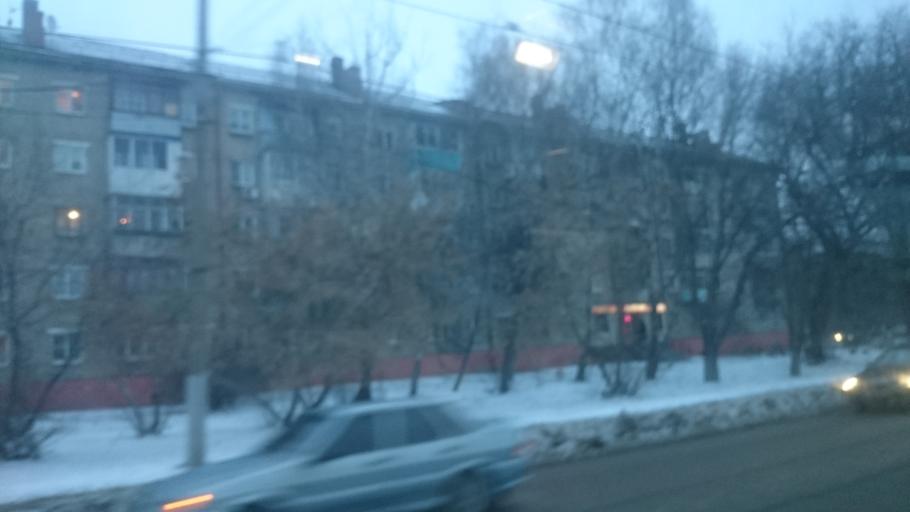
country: RU
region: Tula
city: Tula
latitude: 54.1886
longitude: 37.6231
